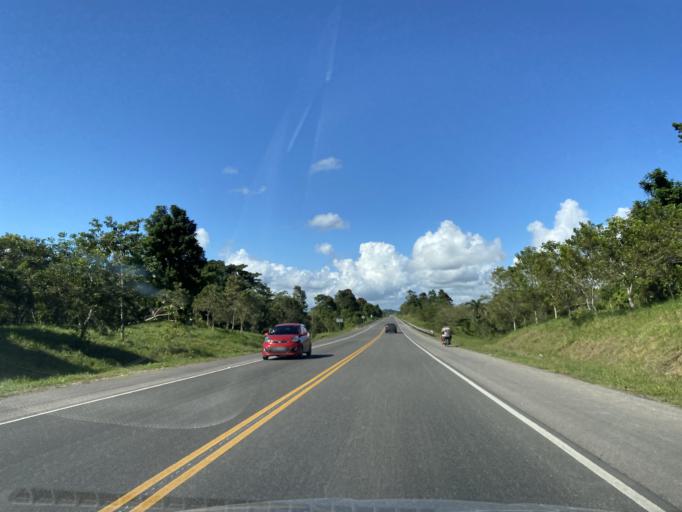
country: DO
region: Monte Plata
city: Sabana Grande de Boya
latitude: 18.9890
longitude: -69.8119
